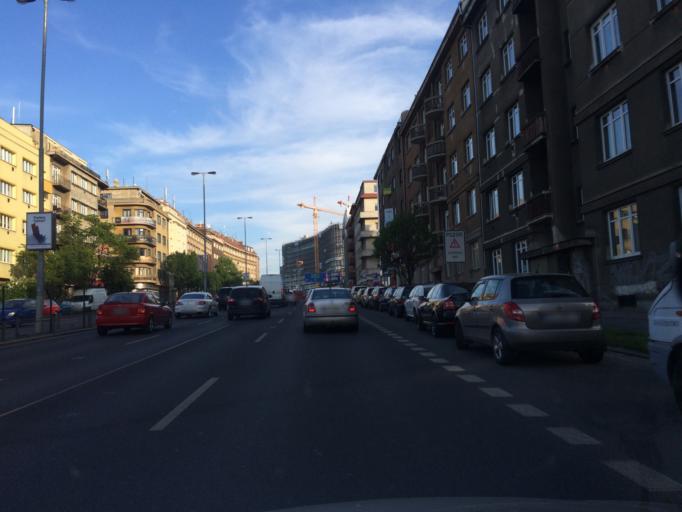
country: CZ
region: Praha
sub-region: Praha 2
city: Vysehrad
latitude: 50.0553
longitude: 14.4379
